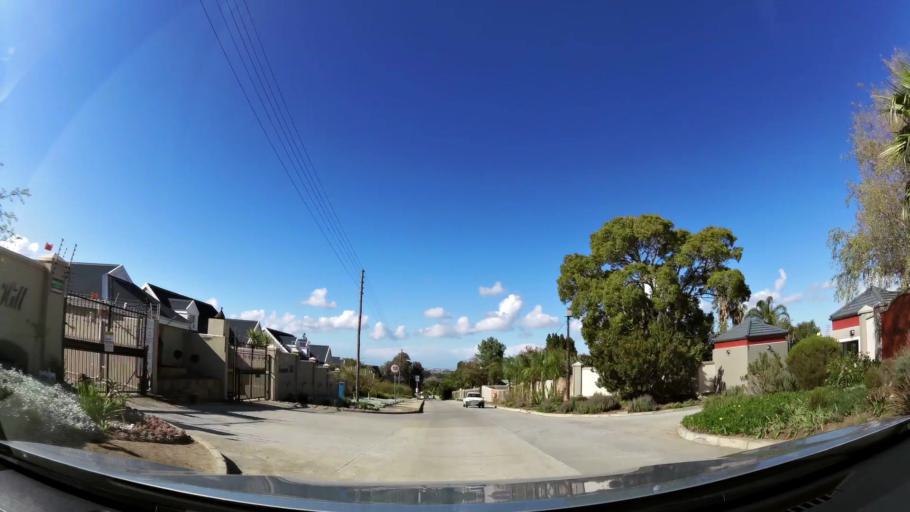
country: ZA
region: Western Cape
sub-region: Eden District Municipality
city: George
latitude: -33.9428
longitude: 22.4076
